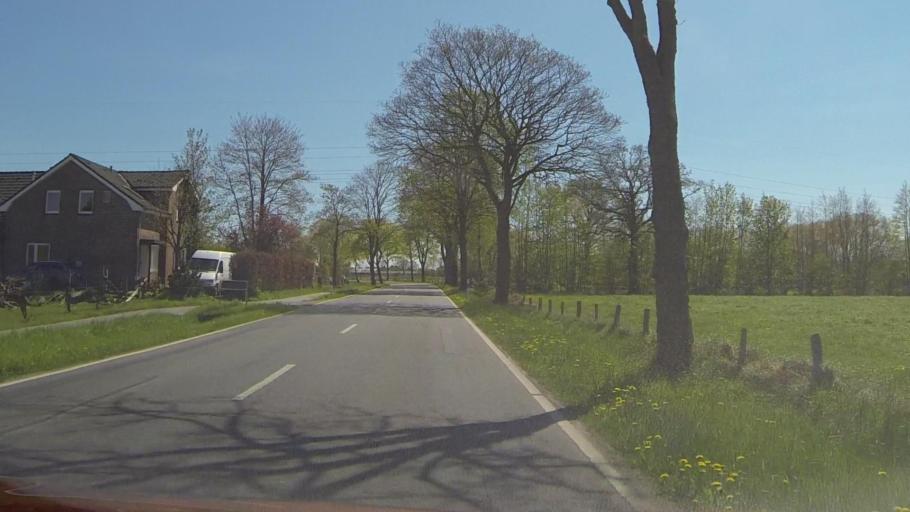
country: DE
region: Schleswig-Holstein
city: Ellerbek
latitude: 53.6526
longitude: 9.8700
